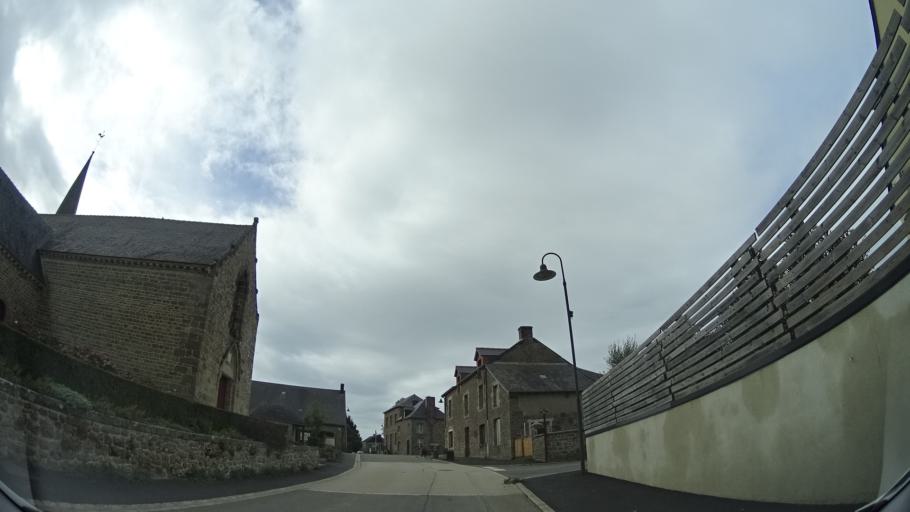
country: FR
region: Brittany
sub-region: Departement d'Ille-et-Vilaine
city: Tinteniac
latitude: 48.2859
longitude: -1.8887
